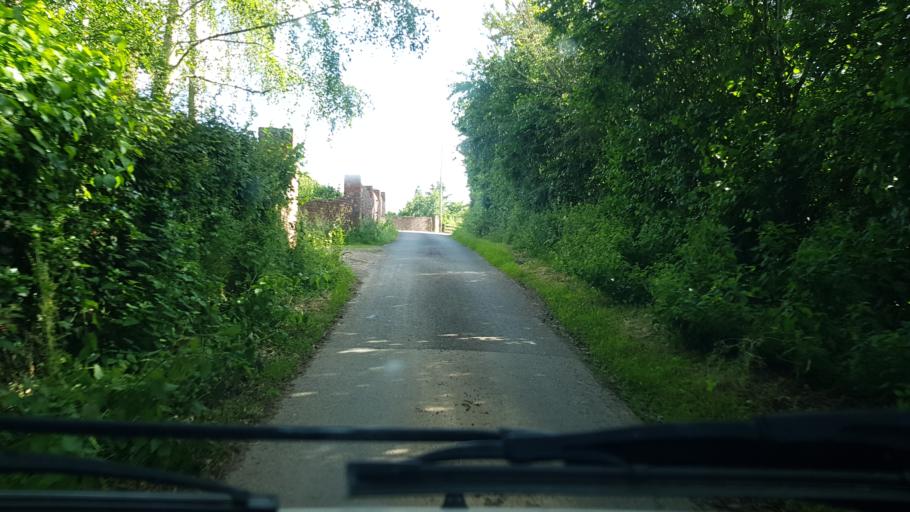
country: GB
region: England
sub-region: Worcestershire
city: Bewdley
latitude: 52.3432
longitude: -2.3299
